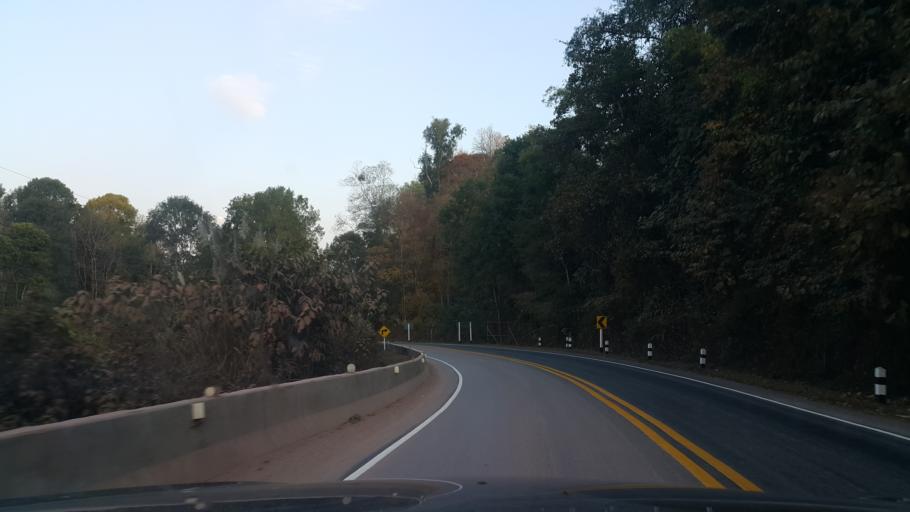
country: TH
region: Loei
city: Phu Ruea
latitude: 17.4629
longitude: 101.5252
